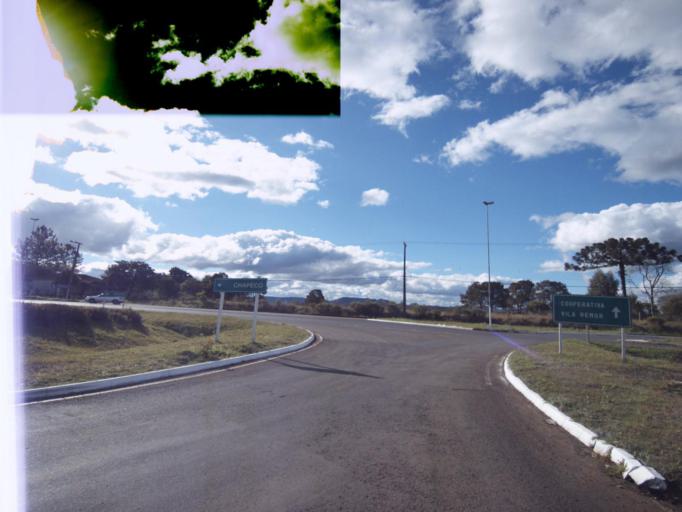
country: BR
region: Santa Catarina
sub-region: Joacaba
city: Joacaba
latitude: -27.1787
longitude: -51.5417
